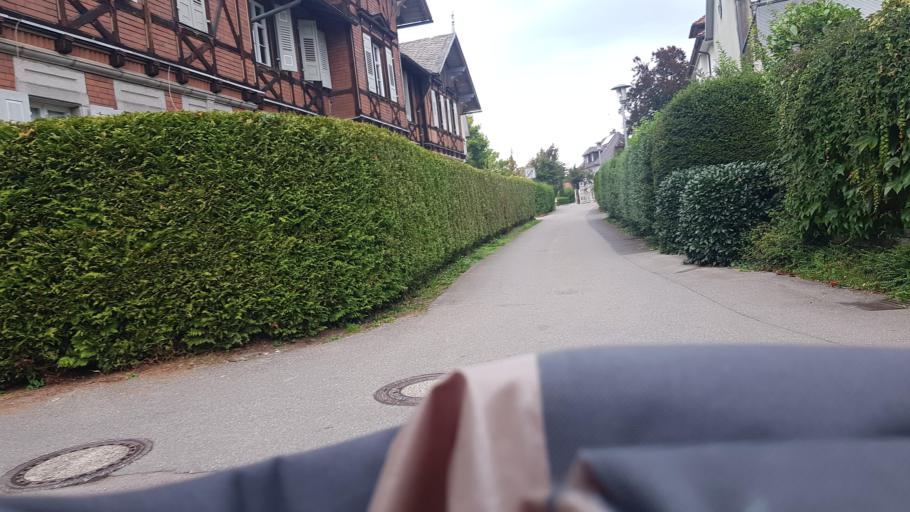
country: DE
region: Bavaria
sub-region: Swabia
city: Bodolz
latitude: 47.5595
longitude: 9.6683
